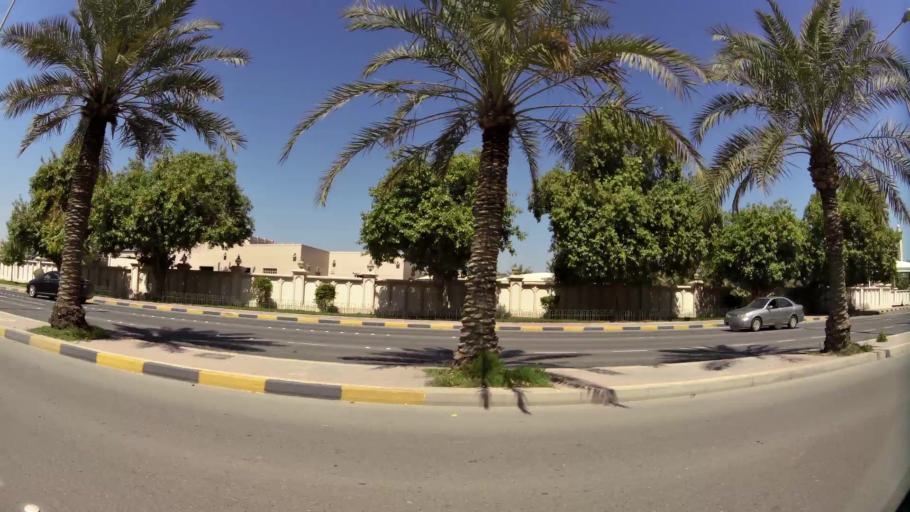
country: BH
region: Manama
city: Manama
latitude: 26.2167
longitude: 50.5942
